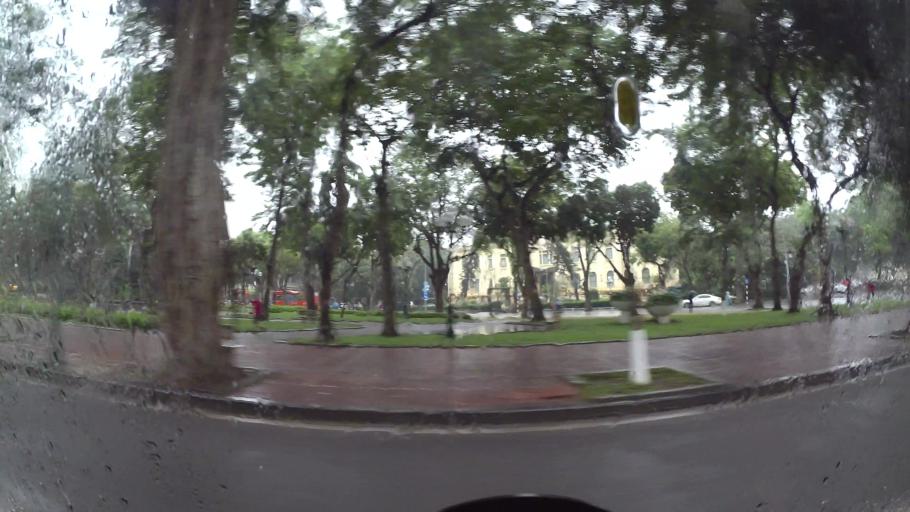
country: VN
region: Ha Noi
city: Hoan Kiem
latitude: 21.0267
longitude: 105.8561
